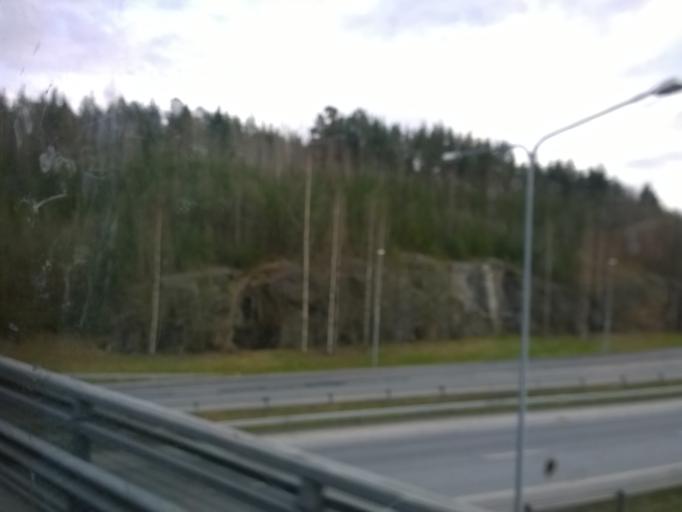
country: FI
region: Pirkanmaa
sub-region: Tampere
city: Tampere
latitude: 61.4664
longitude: 23.7715
